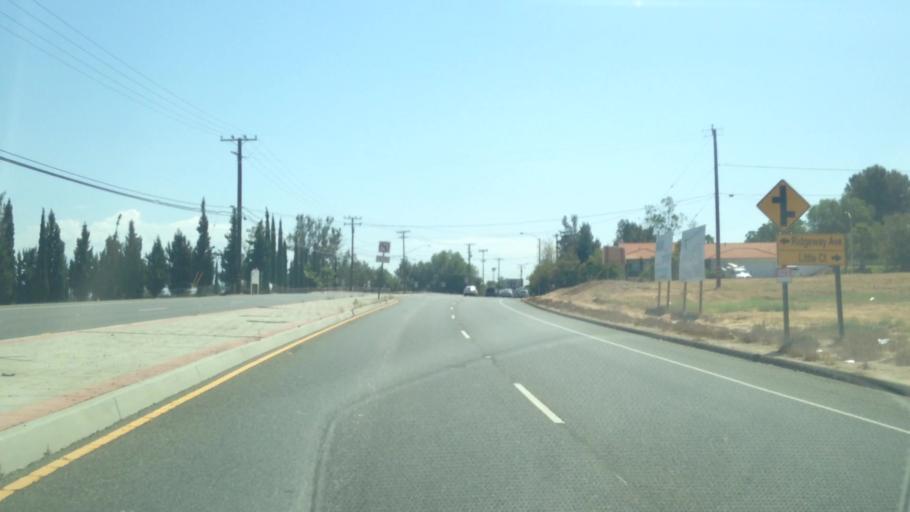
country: US
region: California
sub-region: Riverside County
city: Woodcrest
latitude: 33.8868
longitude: -117.3466
